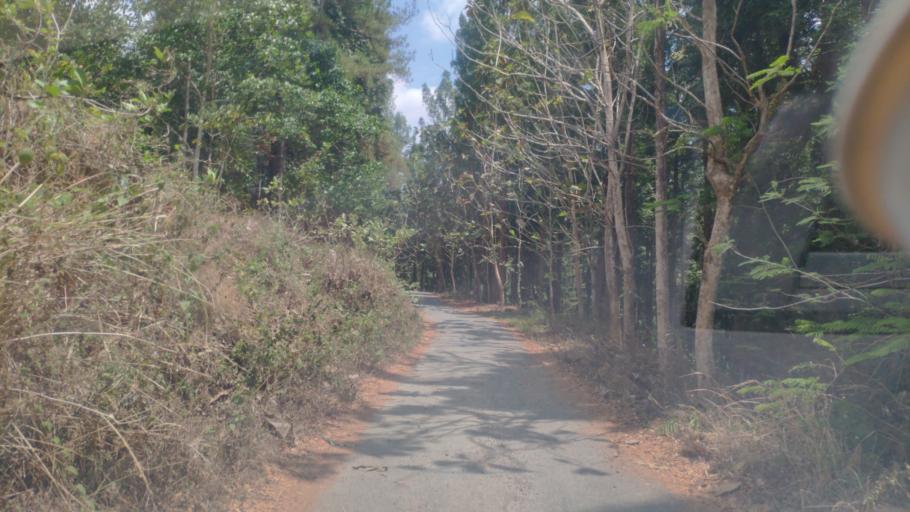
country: ID
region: Central Java
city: Gombong
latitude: -7.4843
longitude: 109.6160
